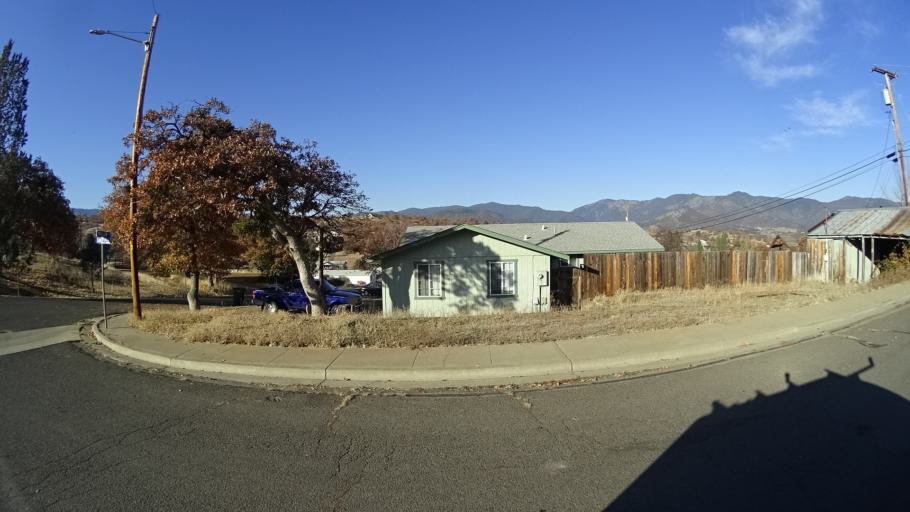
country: US
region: California
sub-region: Siskiyou County
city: Yreka
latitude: 41.7070
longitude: -122.6169
